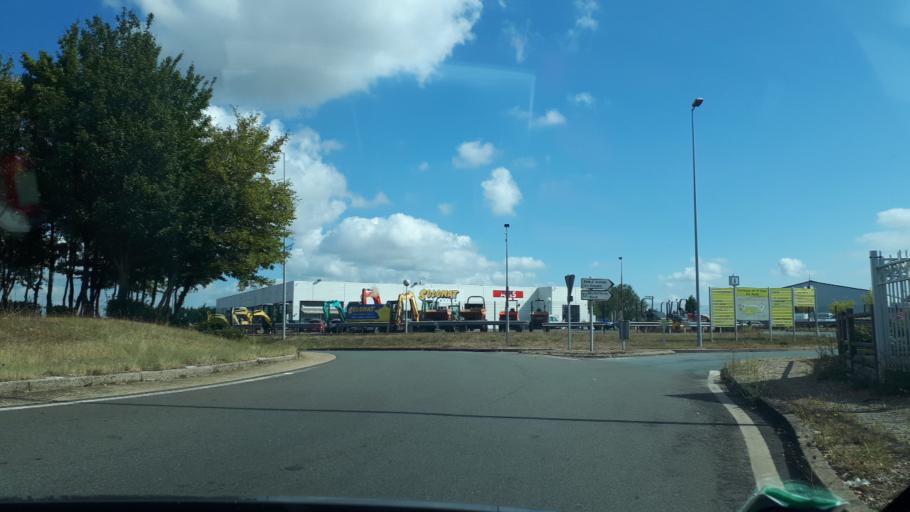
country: FR
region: Centre
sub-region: Departement du Loir-et-Cher
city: Saint-Ouen
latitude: 47.8180
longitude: 1.0760
